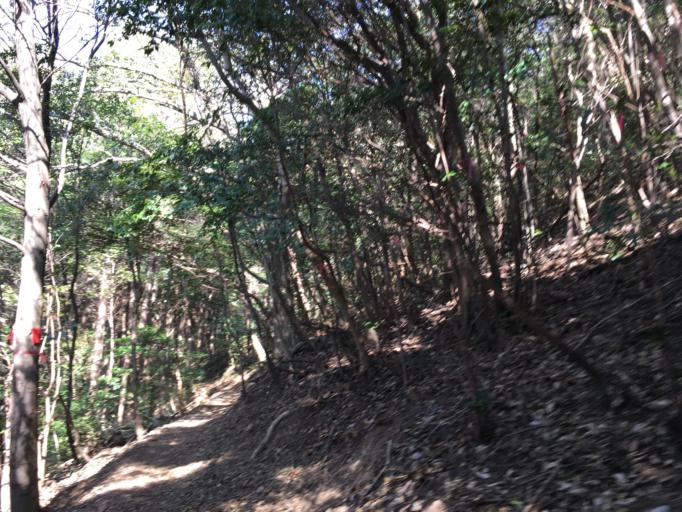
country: JP
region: Aichi
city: Toyohashi
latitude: 34.7352
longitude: 137.4399
